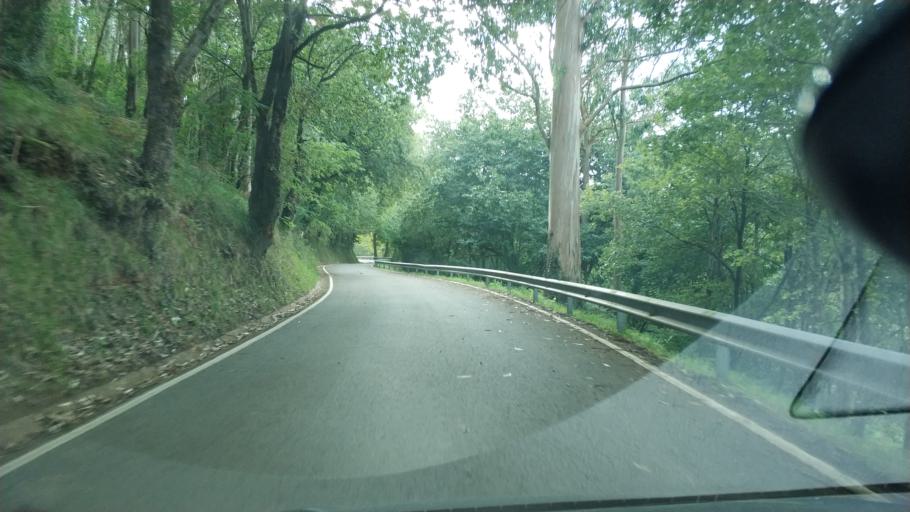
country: ES
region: Cantabria
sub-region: Provincia de Cantabria
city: Santa Maria de Cayon
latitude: 43.2901
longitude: -3.8267
